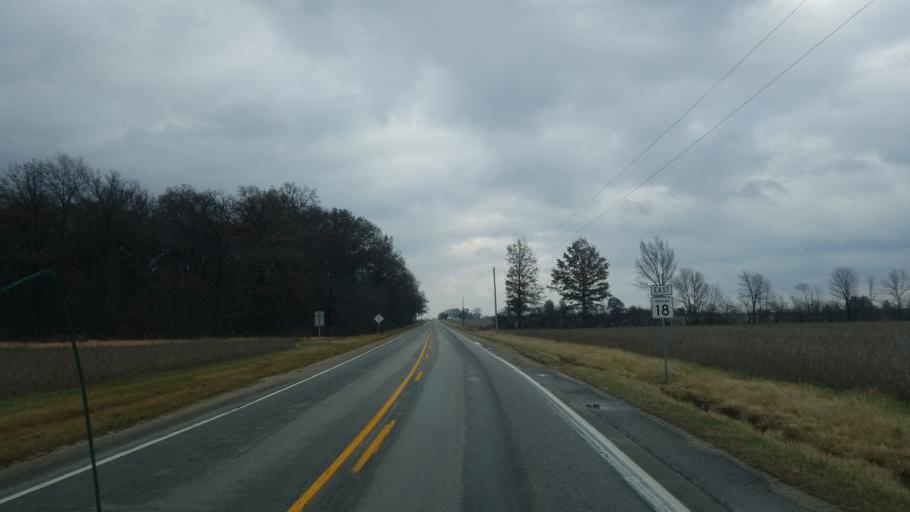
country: US
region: Indiana
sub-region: Adams County
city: Geneva
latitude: 40.5407
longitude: -84.9905
